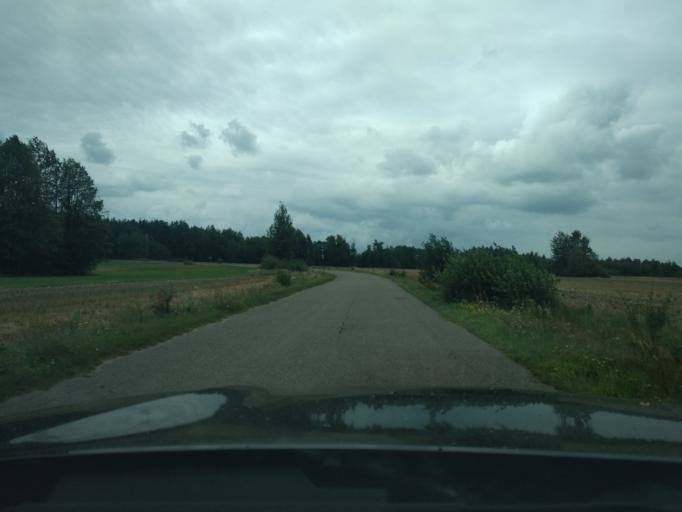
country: PL
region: Masovian Voivodeship
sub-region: Powiat pultuski
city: Obryte
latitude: 52.7457
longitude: 21.2148
